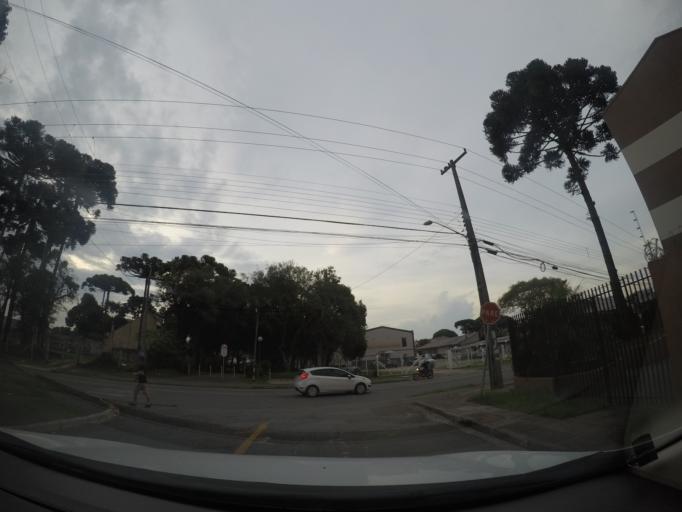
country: BR
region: Parana
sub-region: Sao Jose Dos Pinhais
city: Sao Jose dos Pinhais
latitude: -25.5244
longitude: -49.2346
